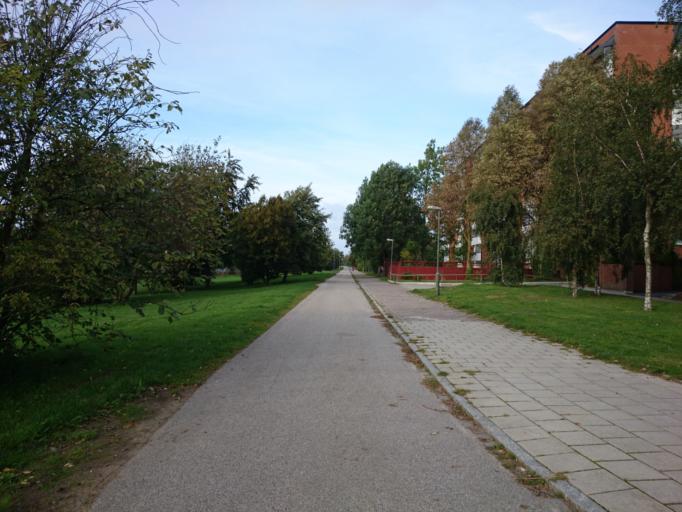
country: SE
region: Skane
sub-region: Malmo
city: Malmoe
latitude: 55.5731
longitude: 12.9714
